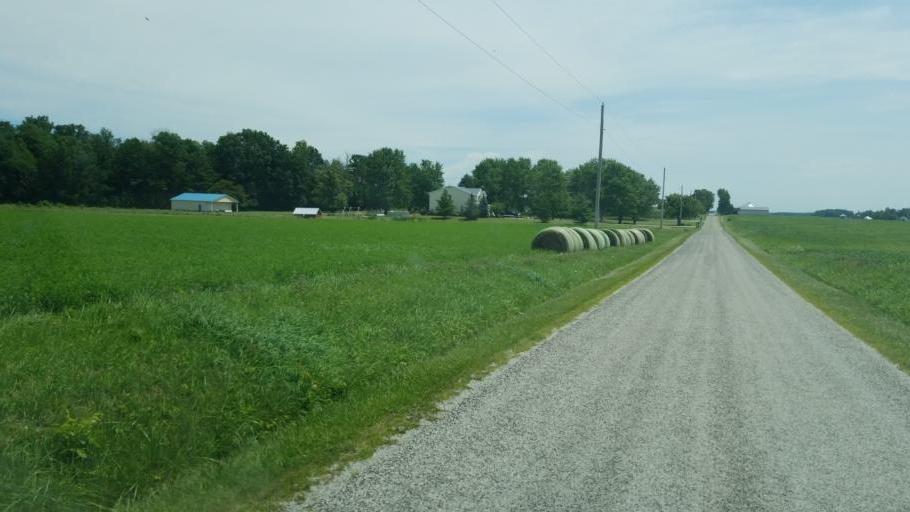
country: US
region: Ohio
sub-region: Crawford County
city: Bucyrus
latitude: 40.8740
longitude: -82.9372
